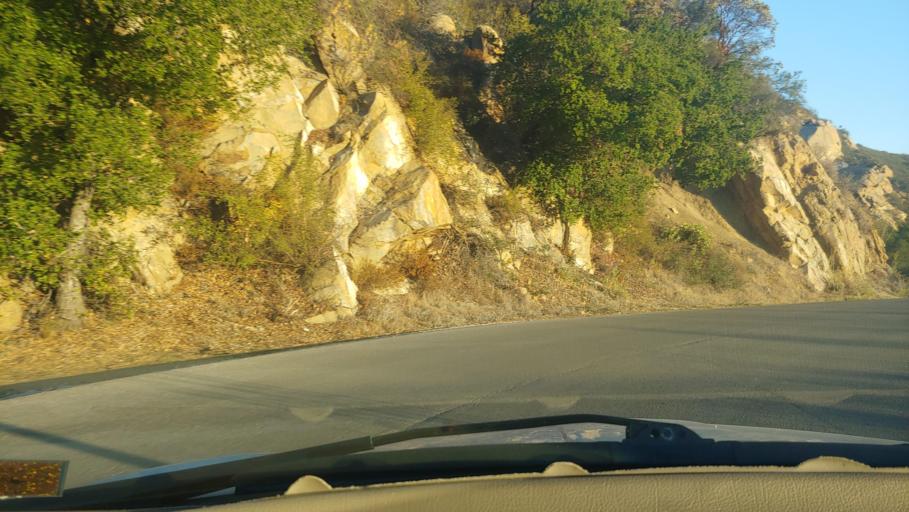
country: US
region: California
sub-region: Santa Barbara County
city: Mission Canyon
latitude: 34.4783
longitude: -119.6802
